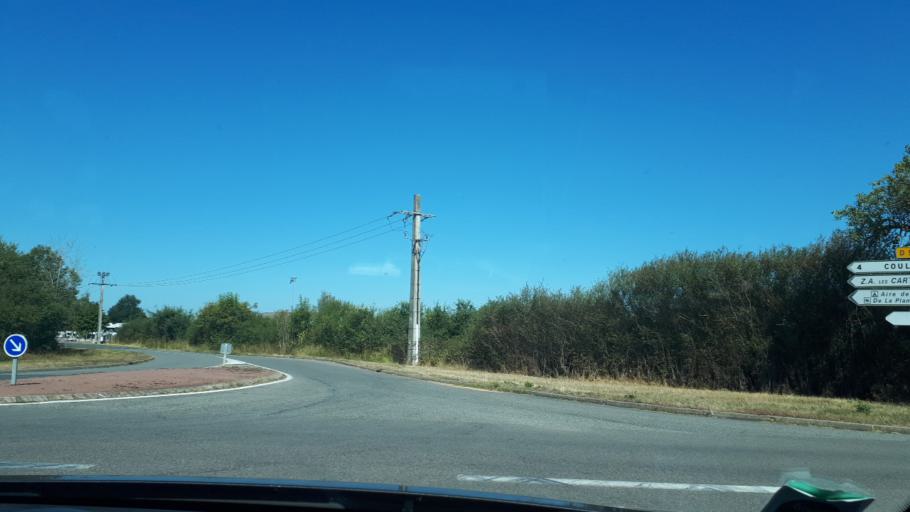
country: FR
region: Centre
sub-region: Departement du Loiret
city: Coullons
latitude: 47.6176
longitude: 2.5426
